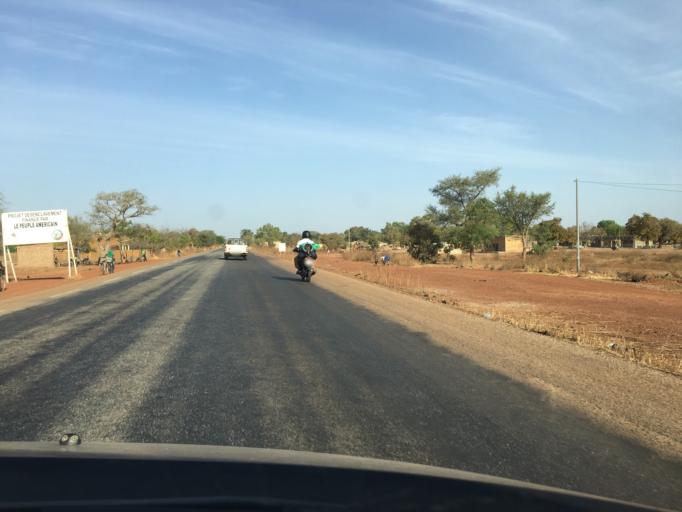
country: BF
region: Plateau-Central
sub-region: Province du Kourweogo
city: Bousse
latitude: 12.5342
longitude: -1.7815
